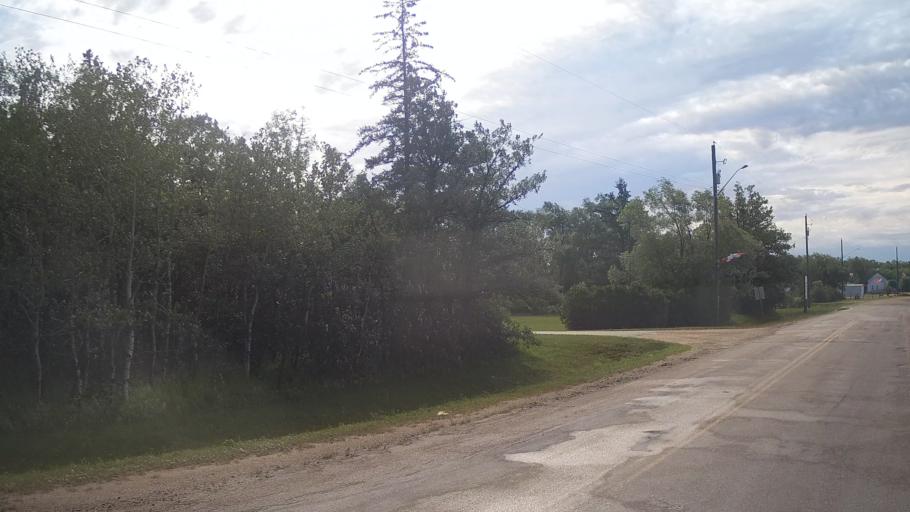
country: CA
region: Manitoba
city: Stonewall
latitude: 50.2051
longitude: -97.6576
